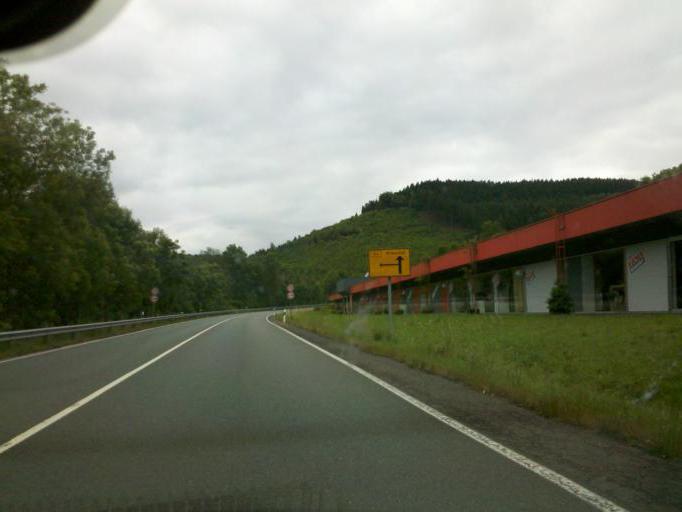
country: DE
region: North Rhine-Westphalia
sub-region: Regierungsbezirk Arnsberg
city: Olpe
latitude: 51.0349
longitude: 7.8926
